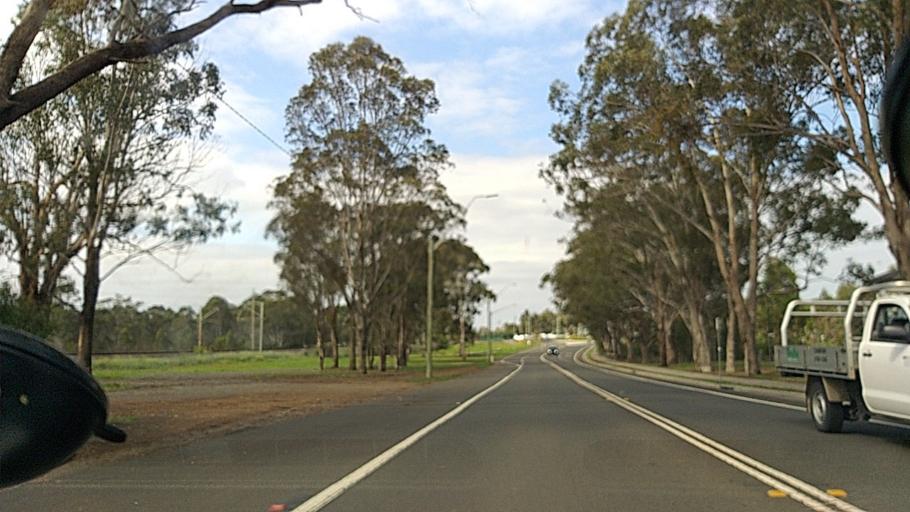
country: AU
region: New South Wales
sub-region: Campbelltown Municipality
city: Glen Alpine
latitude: -34.0739
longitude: 150.7903
